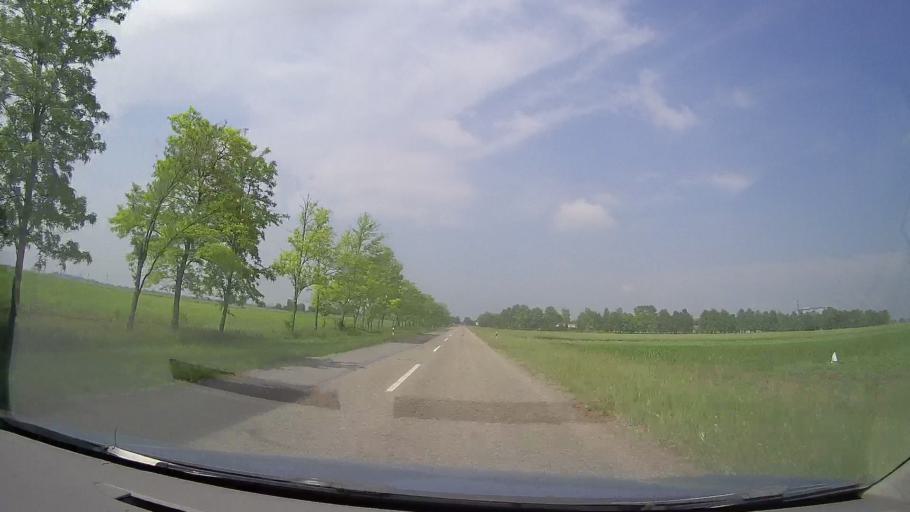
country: RS
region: Autonomna Pokrajina Vojvodina
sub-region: Juznobanatski Okrug
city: Kovacica
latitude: 45.1105
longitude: 20.6472
